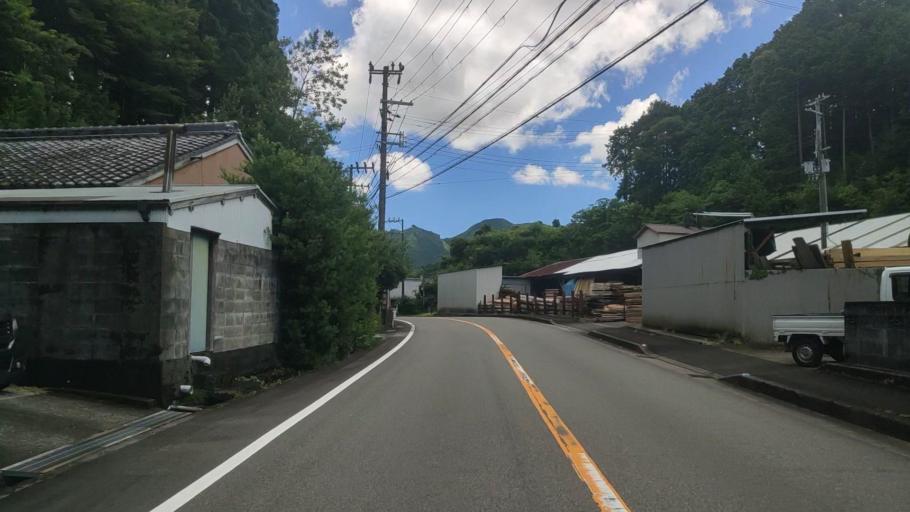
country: JP
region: Mie
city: Owase
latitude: 33.9508
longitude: 136.0697
